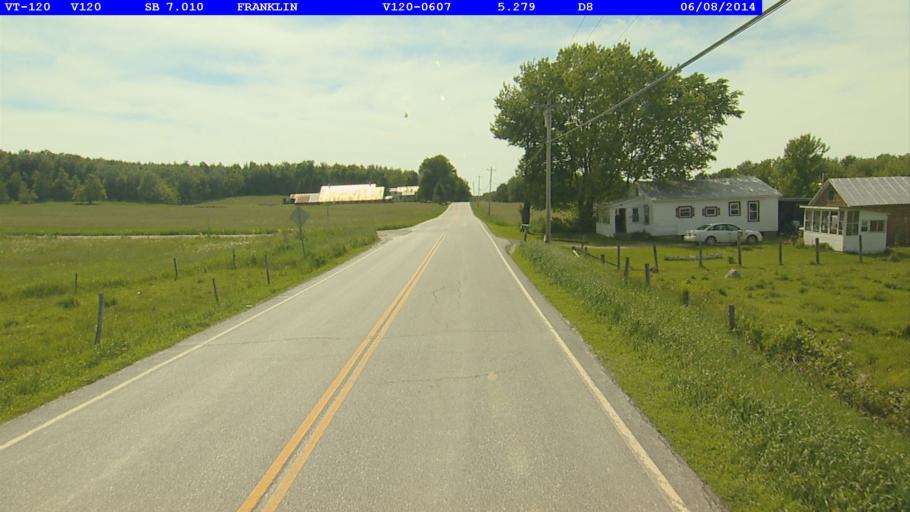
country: US
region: Vermont
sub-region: Franklin County
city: Enosburg Falls
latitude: 44.9864
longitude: -72.8877
